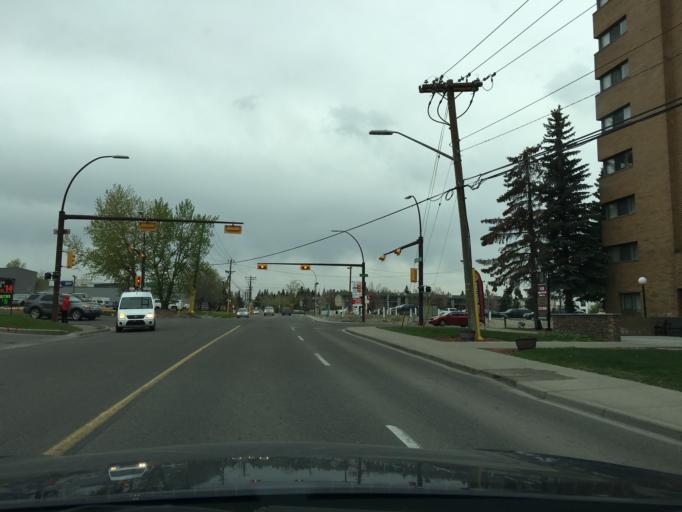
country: CA
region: Alberta
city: Calgary
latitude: 50.9718
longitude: -114.0688
